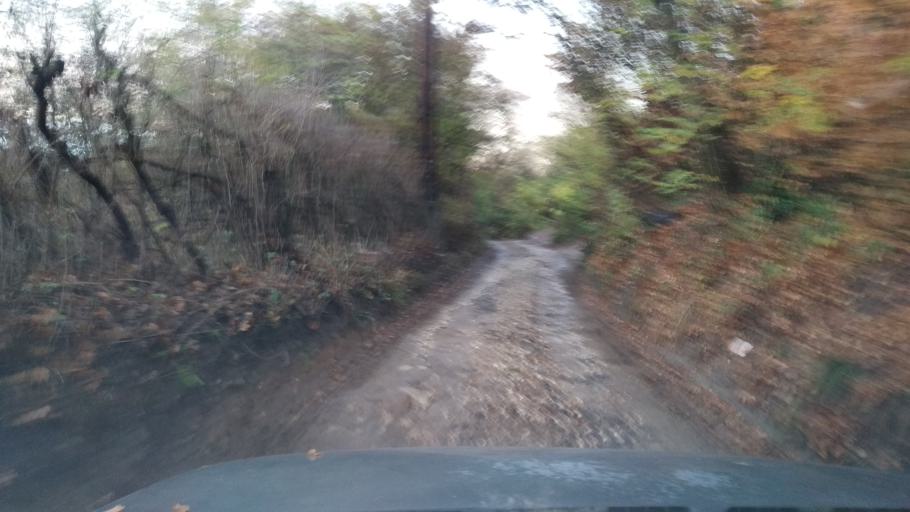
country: HU
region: Pest
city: Nagykovacsi
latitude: 47.6577
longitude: 18.9986
